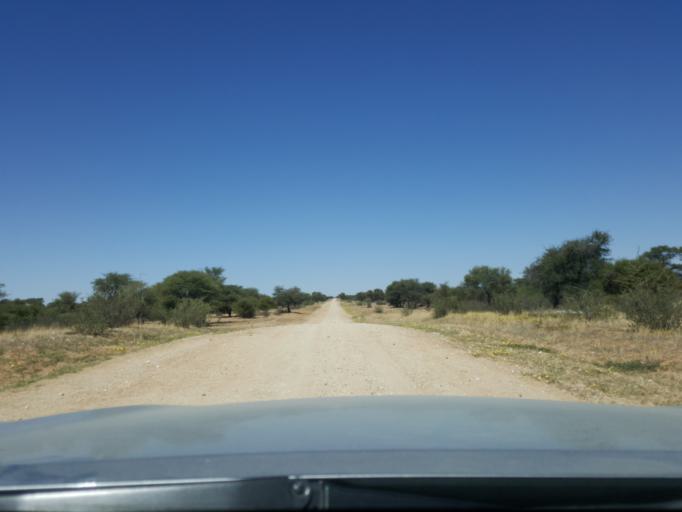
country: BW
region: Kgalagadi
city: Hukuntsi
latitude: -24.0582
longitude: 21.2224
